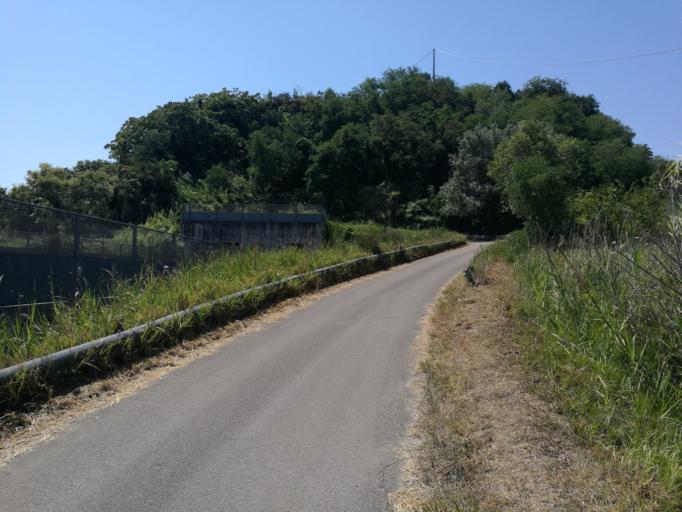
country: IT
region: Abruzzo
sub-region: Provincia di Chieti
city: Ortona
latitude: 42.3432
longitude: 14.4115
